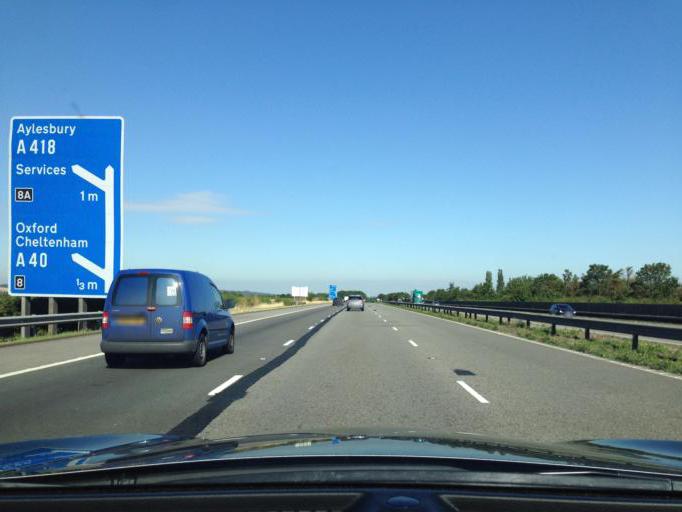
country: GB
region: England
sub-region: Oxfordshire
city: Chalgrove
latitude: 51.7286
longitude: -1.0672
